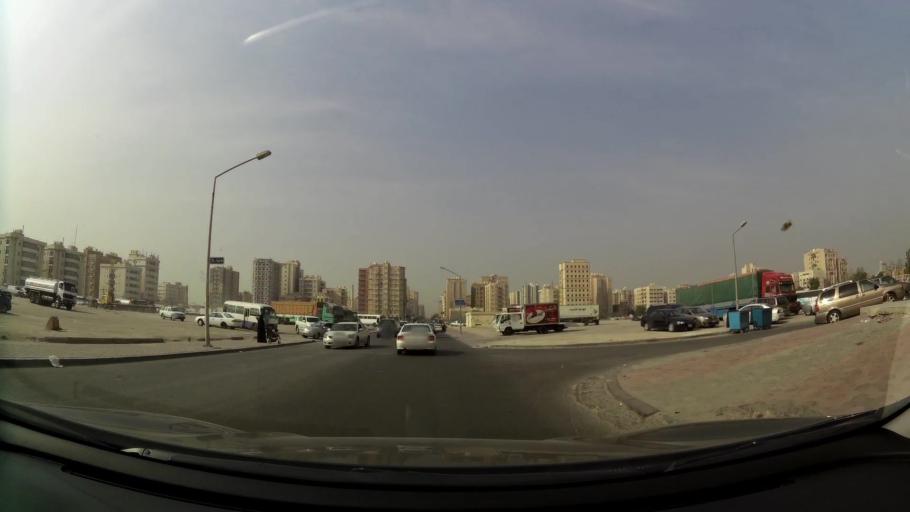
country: KW
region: Al Farwaniyah
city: Al Farwaniyah
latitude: 29.2708
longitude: 47.9582
